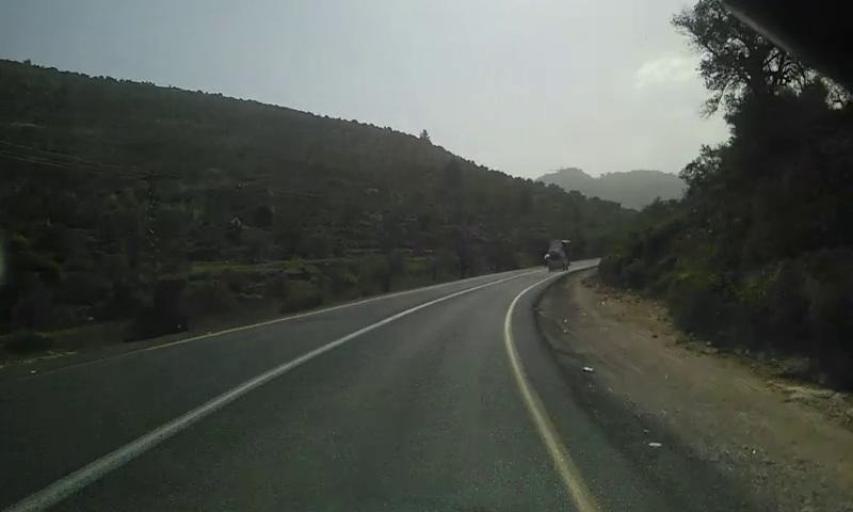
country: PS
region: West Bank
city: Silwad
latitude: 31.9979
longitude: 35.2397
